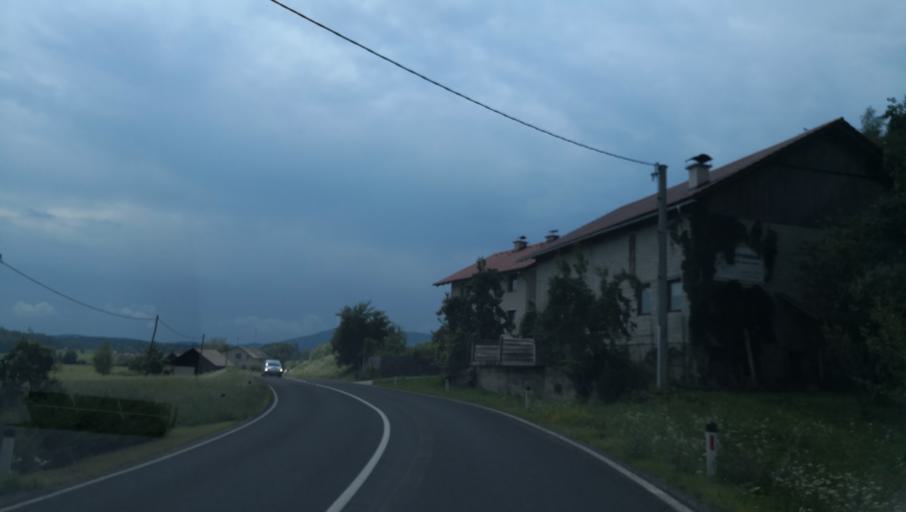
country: SI
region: Ivancna Gorica
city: Ivancna Gorica
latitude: 45.9149
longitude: 14.8019
